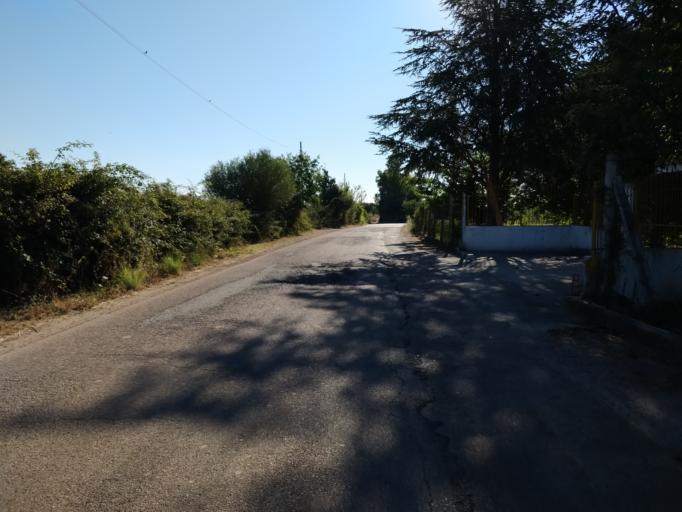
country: IT
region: Sardinia
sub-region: Provincia di Ogliastra
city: Girasole
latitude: 39.9524
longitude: 9.6699
